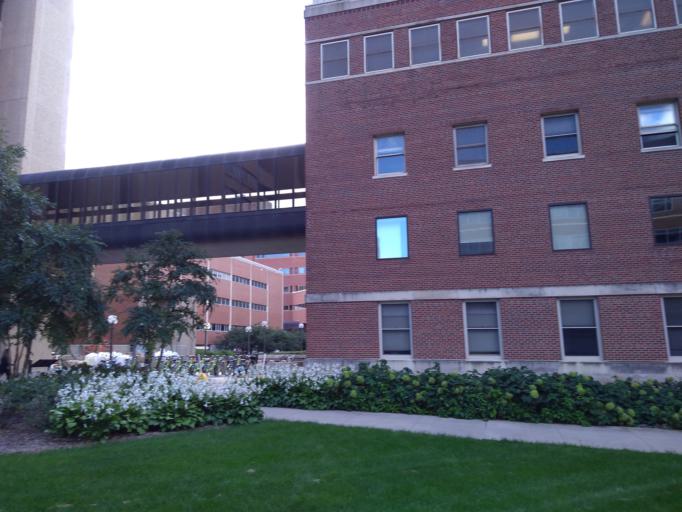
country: US
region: Minnesota
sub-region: Hennepin County
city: Minneapolis
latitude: 44.9725
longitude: -93.2321
